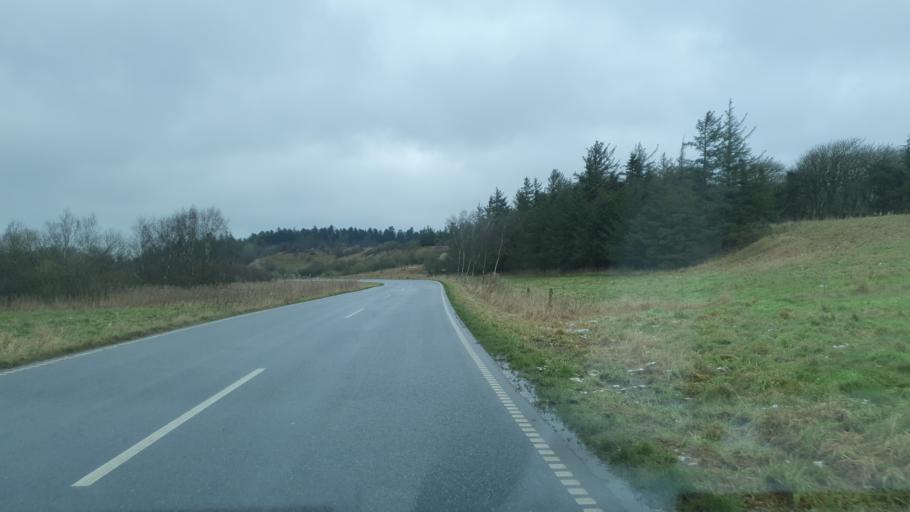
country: DK
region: North Denmark
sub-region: Jammerbugt Kommune
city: Fjerritslev
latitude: 57.1131
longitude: 9.1280
